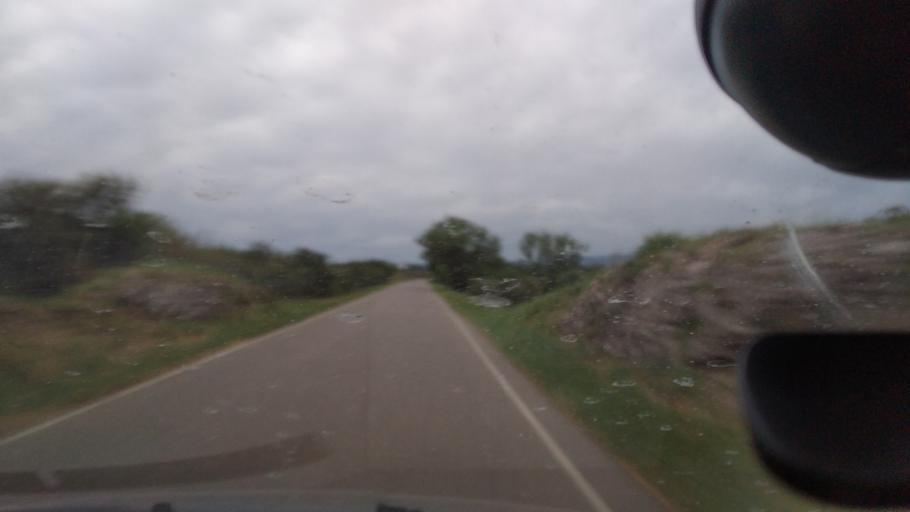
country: AR
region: Cordoba
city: Villa Las Rosas
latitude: -31.8912
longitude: -65.0315
